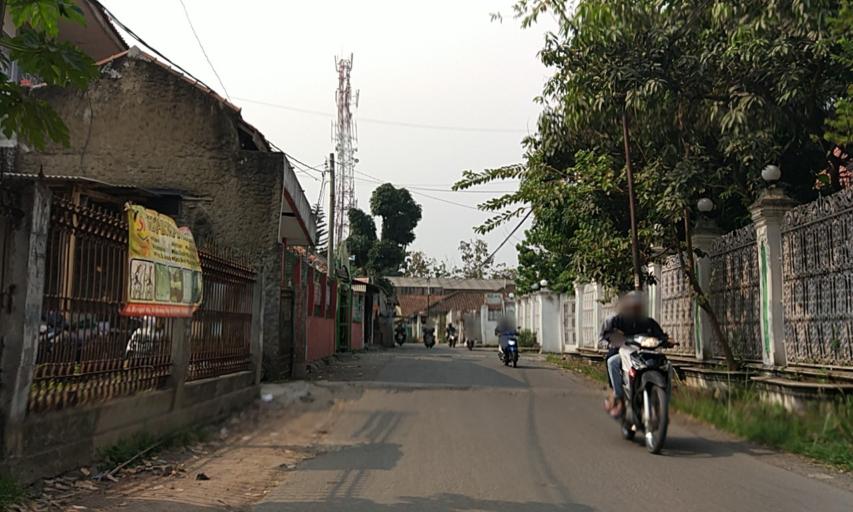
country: ID
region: West Java
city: Margahayukencana
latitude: -6.9691
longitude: 107.5589
